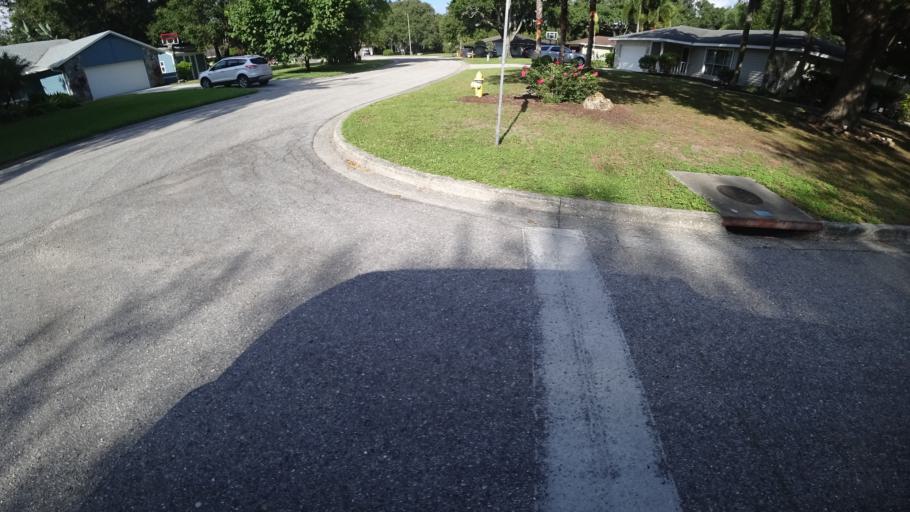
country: US
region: Florida
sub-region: Sarasota County
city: Desoto Lakes
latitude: 27.4323
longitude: -82.4526
